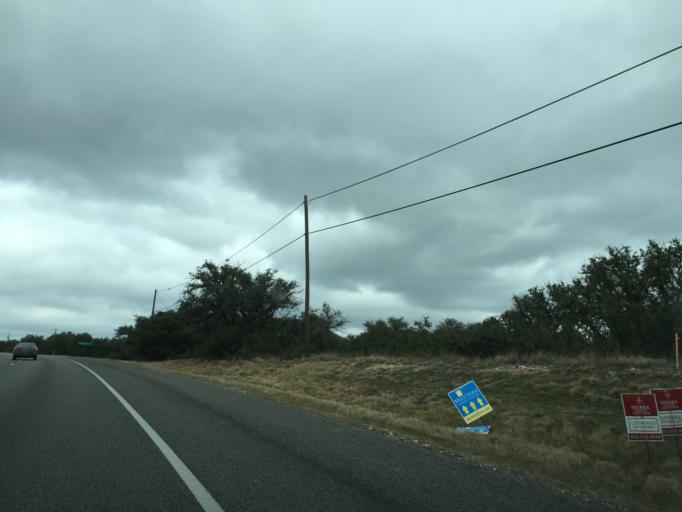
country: US
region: Texas
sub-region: Travis County
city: Briarcliff
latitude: 30.3466
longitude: -98.0506
